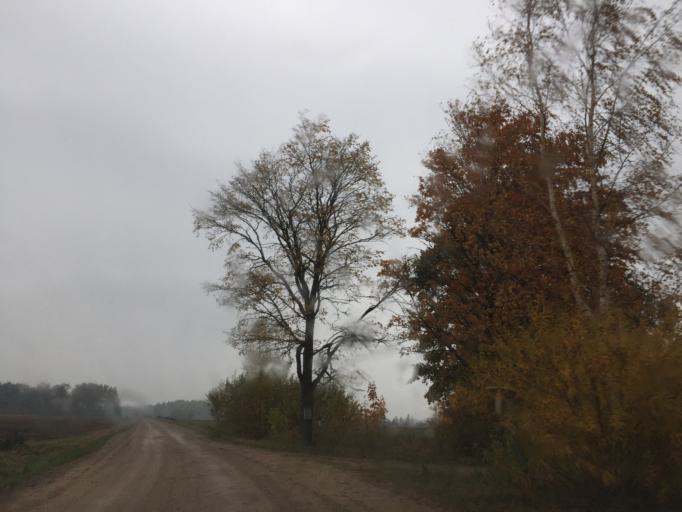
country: LV
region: Dobeles Rajons
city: Dobele
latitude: 56.6721
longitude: 23.4275
